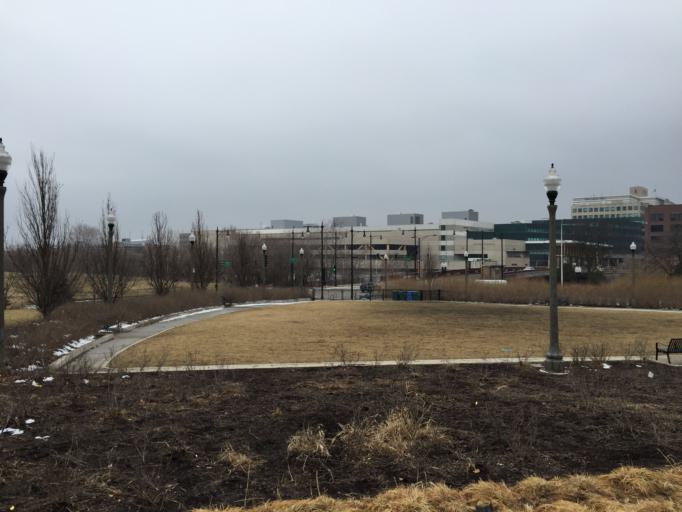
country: US
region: Illinois
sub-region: Cook County
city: Chicago
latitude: 41.8751
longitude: -87.6342
